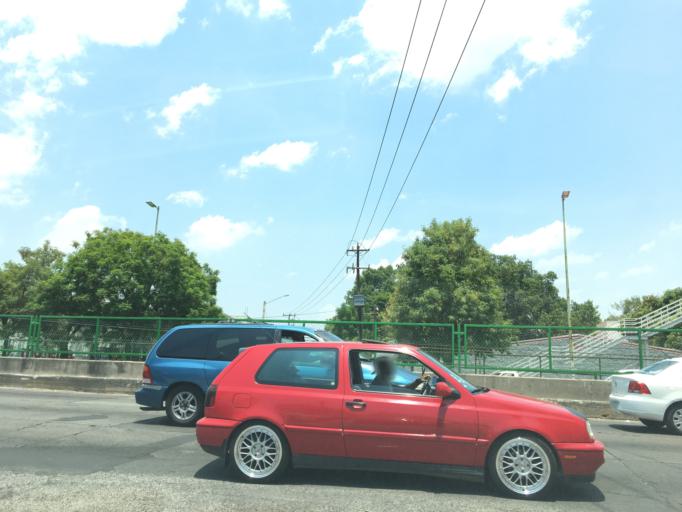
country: MX
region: Jalisco
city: Guadalajara
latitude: 20.6516
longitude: -103.3661
